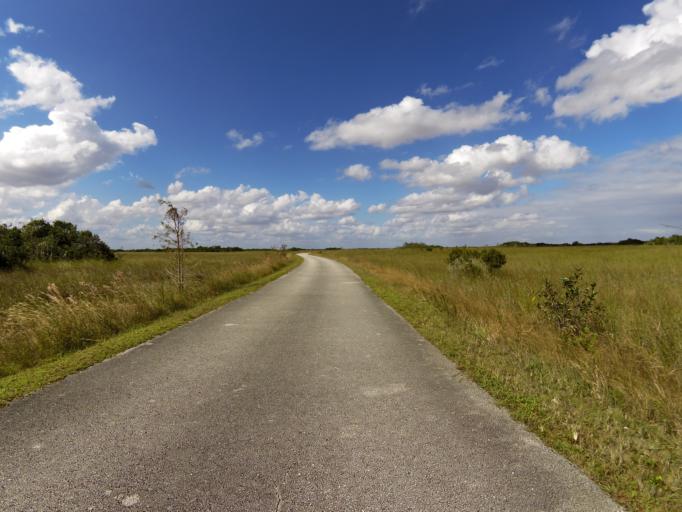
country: US
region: Florida
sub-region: Miami-Dade County
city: The Hammocks
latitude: 25.7274
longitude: -80.7589
